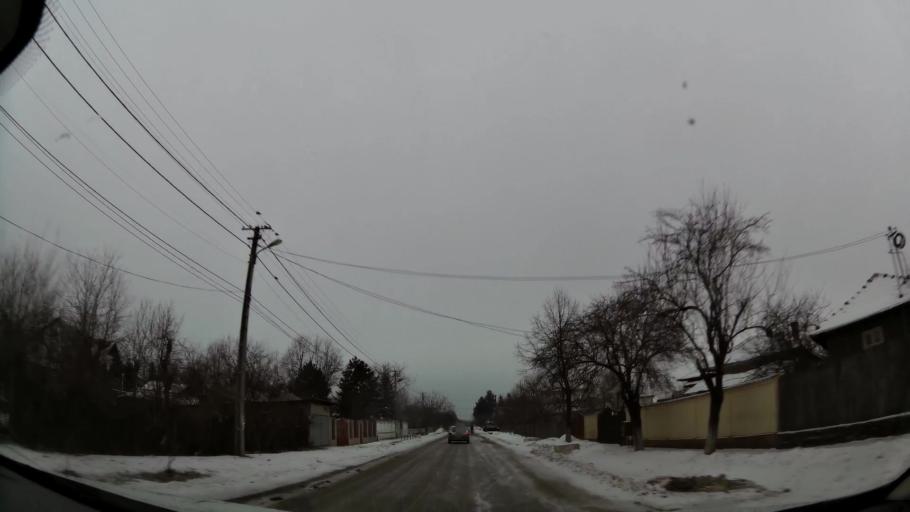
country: RO
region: Prahova
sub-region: Comuna Poenarii-Burchi
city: Ologeni
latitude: 44.7292
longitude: 25.9564
